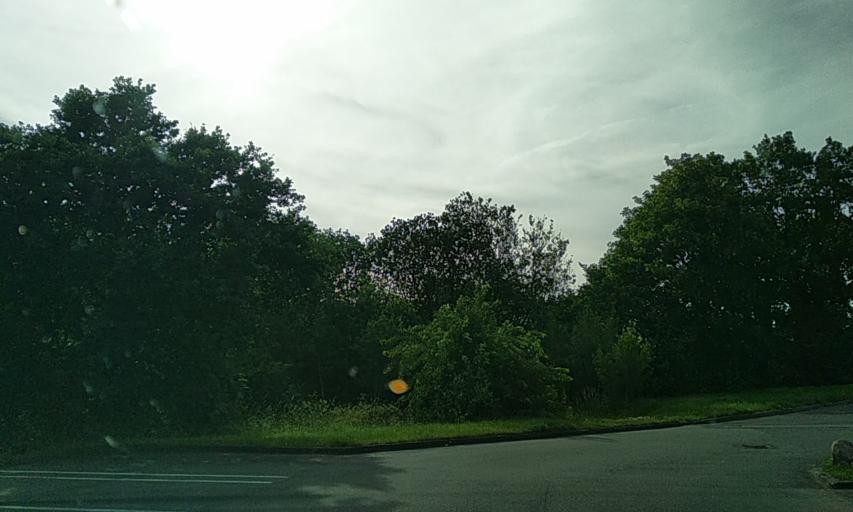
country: DE
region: Schleswig-Holstein
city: Neuberend
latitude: 54.5290
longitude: 9.5259
